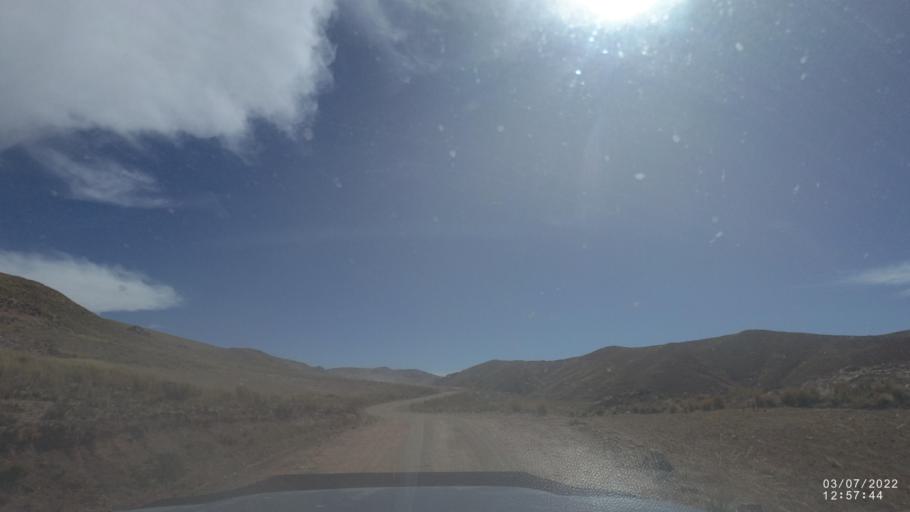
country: BO
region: Cochabamba
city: Sipe Sipe
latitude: -17.7237
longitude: -66.6767
